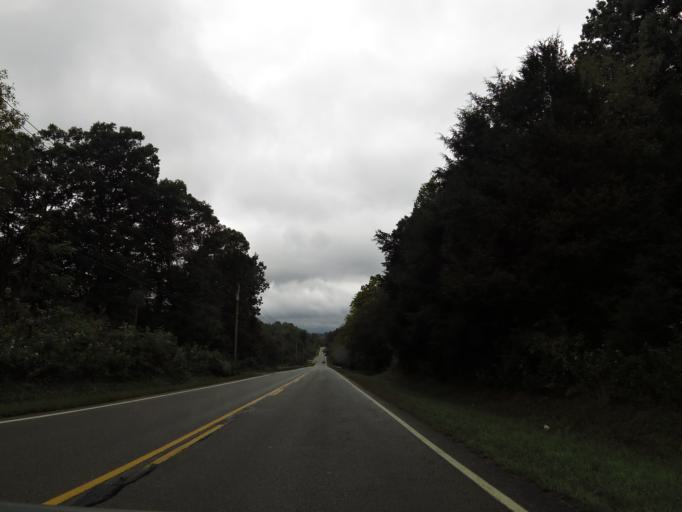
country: US
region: Tennessee
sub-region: Loudon County
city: Loudon
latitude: 35.7711
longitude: -84.3244
